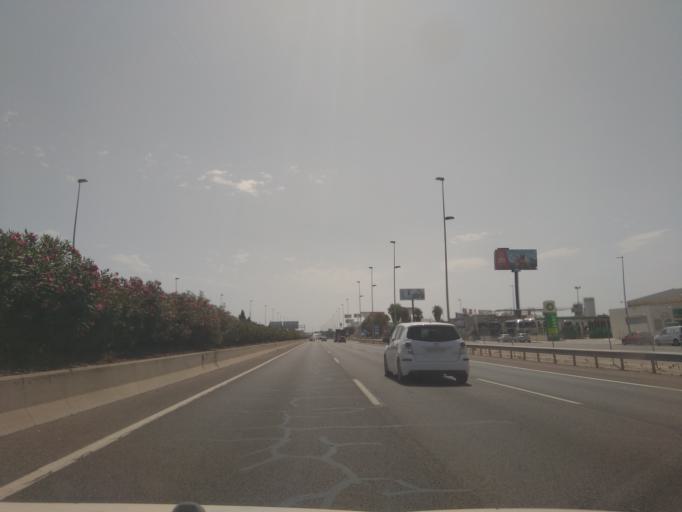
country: ES
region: Valencia
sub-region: Provincia de Valencia
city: Alfafar
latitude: 39.4103
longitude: -0.3805
